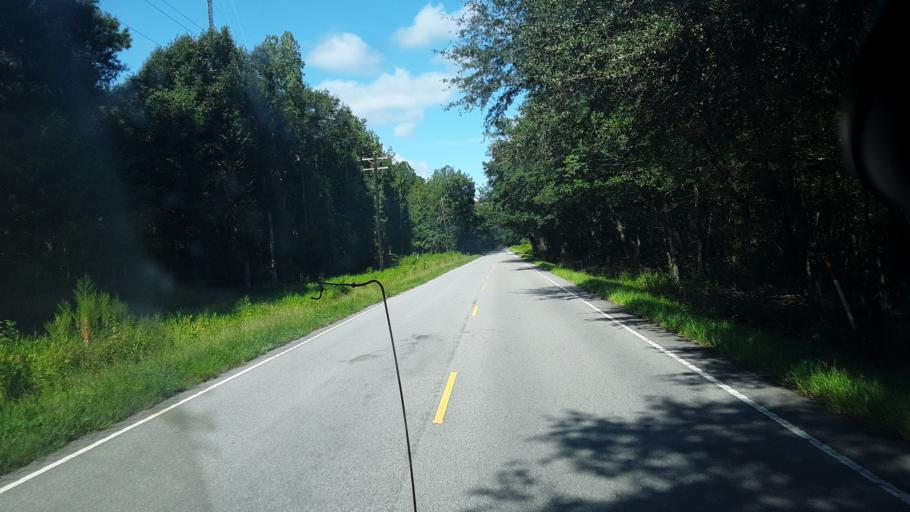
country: US
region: South Carolina
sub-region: Jasper County
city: Ridgeland
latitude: 32.5902
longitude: -80.9649
